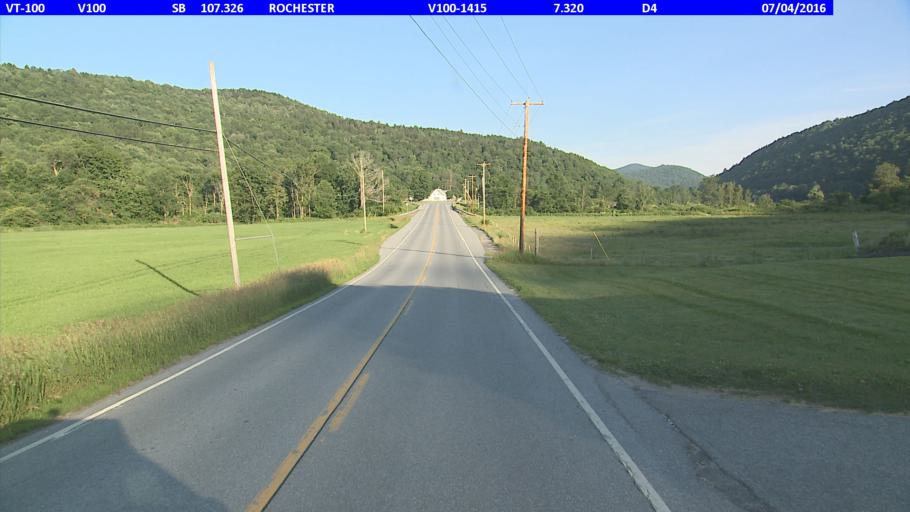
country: US
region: Vermont
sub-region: Orange County
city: Randolph
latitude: 43.8993
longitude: -72.8234
